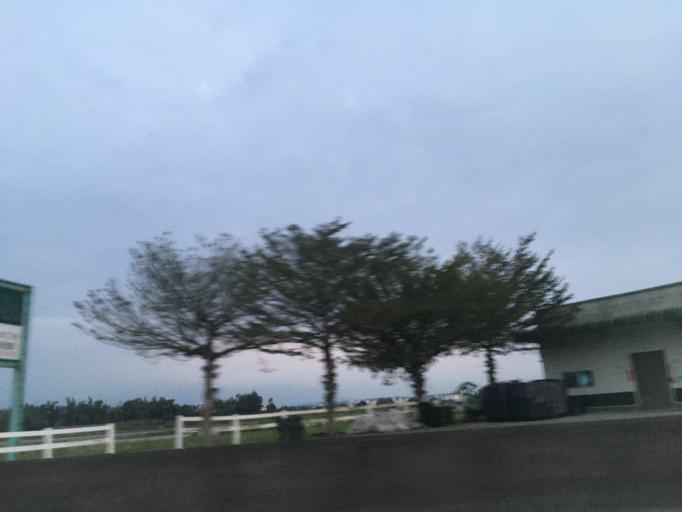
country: TW
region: Taiwan
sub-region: Chiayi
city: Jiayi Shi
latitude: 23.5865
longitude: 120.4646
